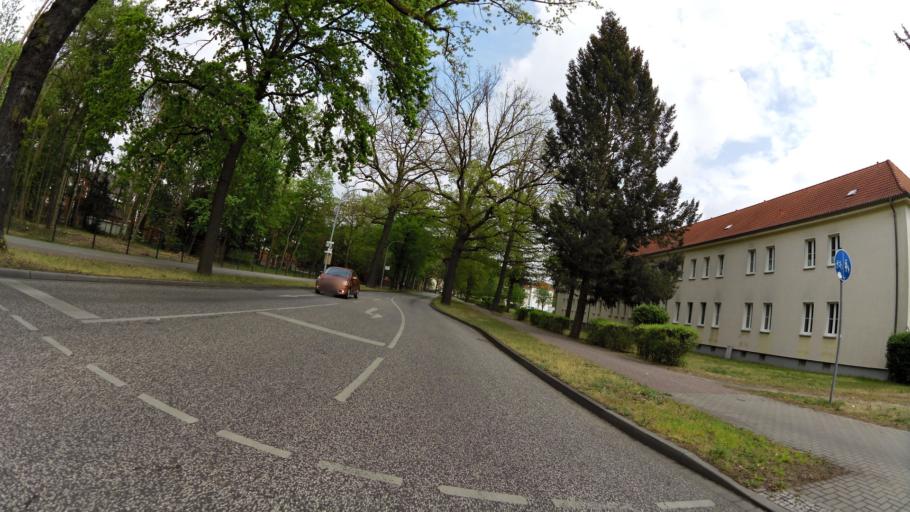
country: DE
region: Brandenburg
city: Konigs Wusterhausen
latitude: 52.2892
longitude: 13.6173
